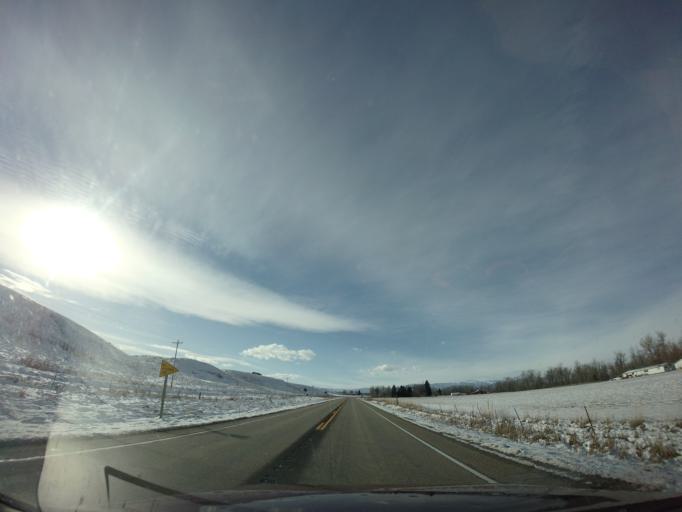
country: US
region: Montana
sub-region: Carbon County
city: Red Lodge
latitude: 45.3873
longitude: -109.1358
